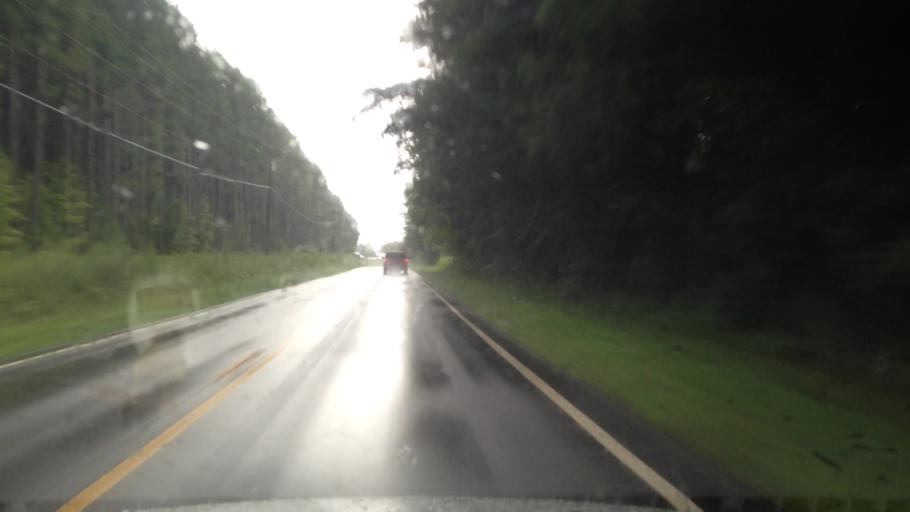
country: US
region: North Carolina
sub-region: Rockingham County
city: Reidsville
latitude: 36.2771
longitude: -79.7365
